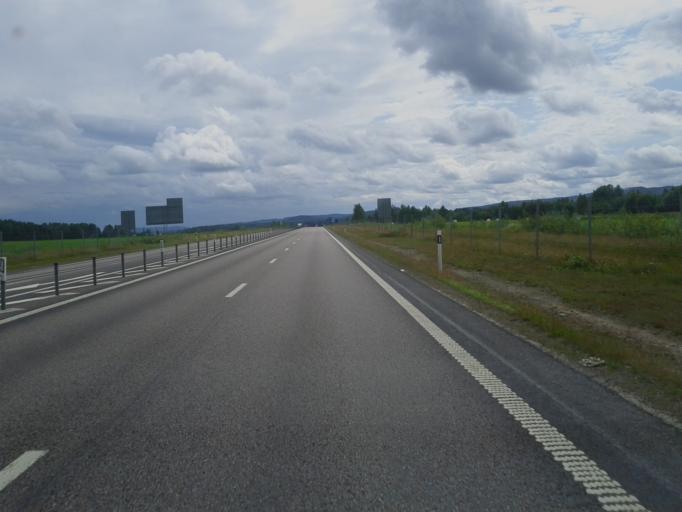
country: SE
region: Dalarna
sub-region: Borlange Kommun
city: Ornas
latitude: 60.4315
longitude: 15.5216
